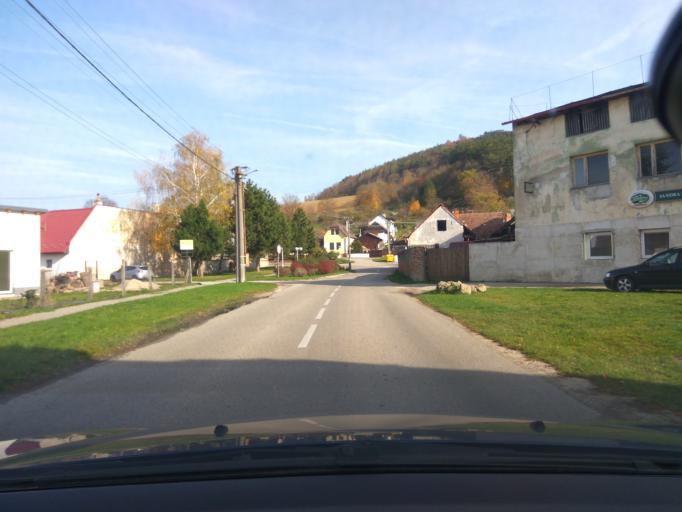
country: SK
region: Nitriansky
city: Brezova pod Bradlom
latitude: 48.6592
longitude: 17.5395
